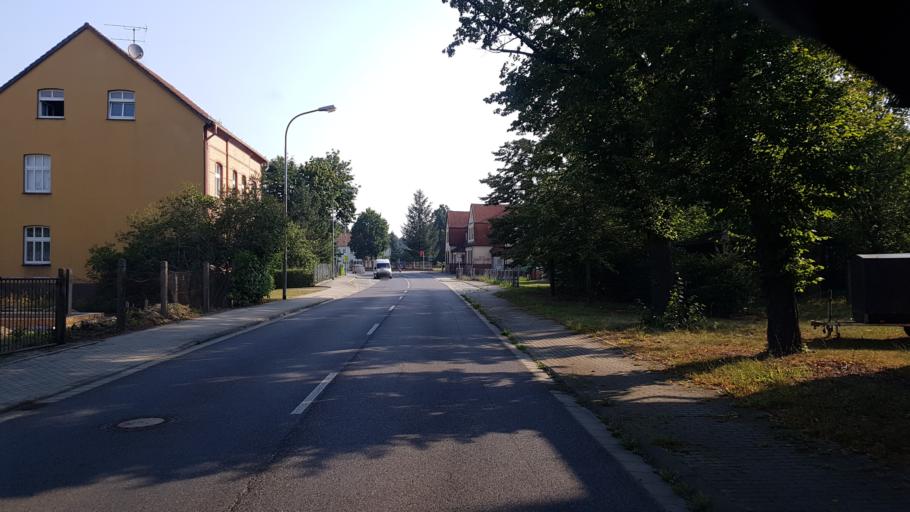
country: DE
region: Brandenburg
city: Drebkau
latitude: 51.6546
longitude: 14.2220
